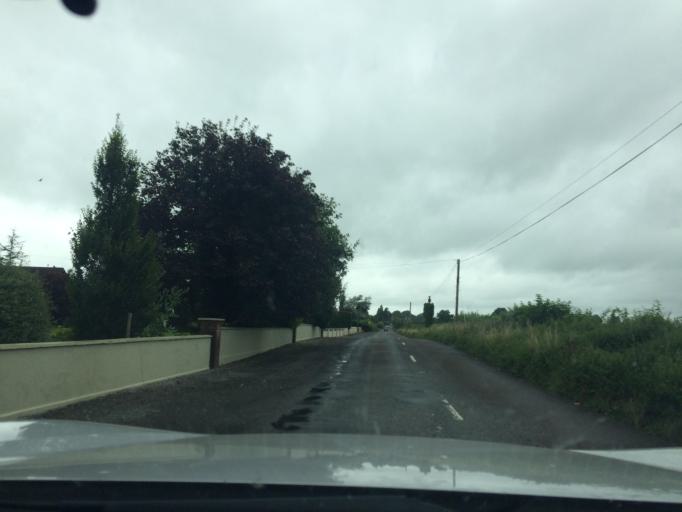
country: IE
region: Munster
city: Thurles
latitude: 52.6182
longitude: -7.8803
